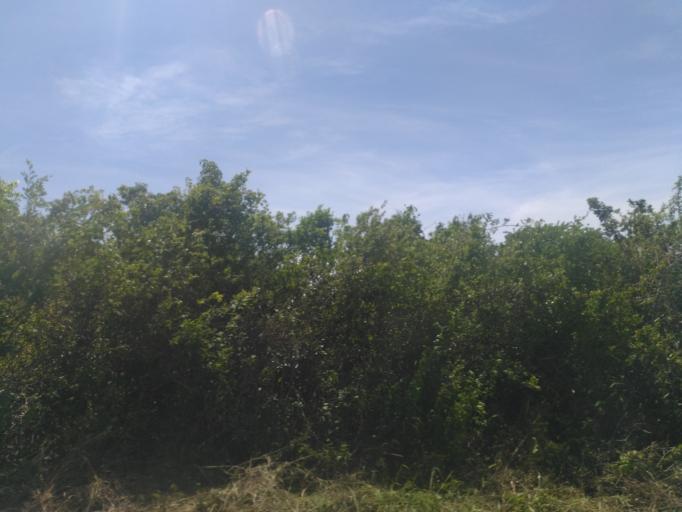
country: TZ
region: Zanzibar North
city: Gamba
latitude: -5.9260
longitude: 39.3493
